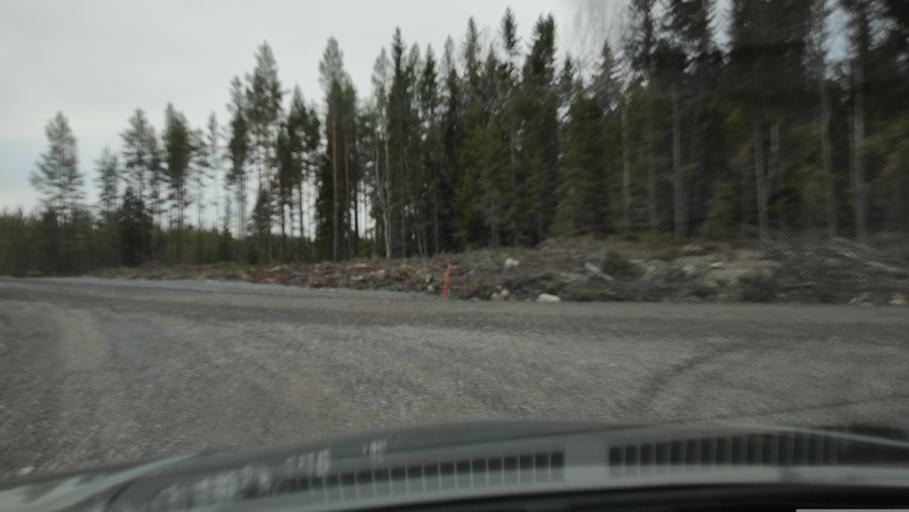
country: FI
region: Ostrobothnia
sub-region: Sydosterbotten
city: Kristinestad
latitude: 62.1956
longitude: 21.5469
